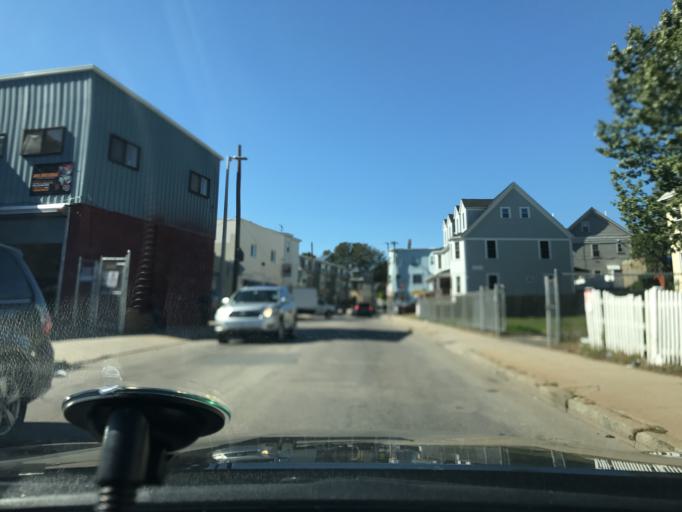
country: US
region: Massachusetts
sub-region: Suffolk County
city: South Boston
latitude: 42.3120
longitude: -71.0721
